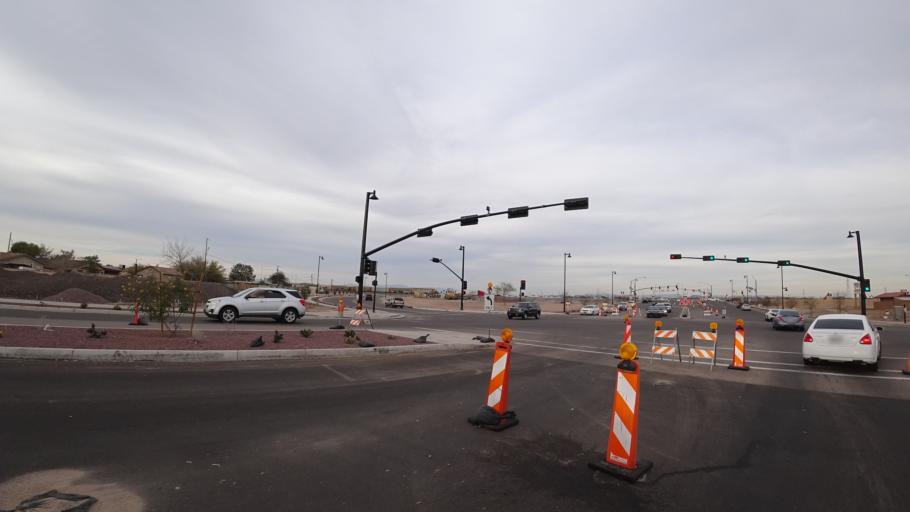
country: US
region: Arizona
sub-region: Maricopa County
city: El Mirage
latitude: 33.6091
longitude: -112.3156
